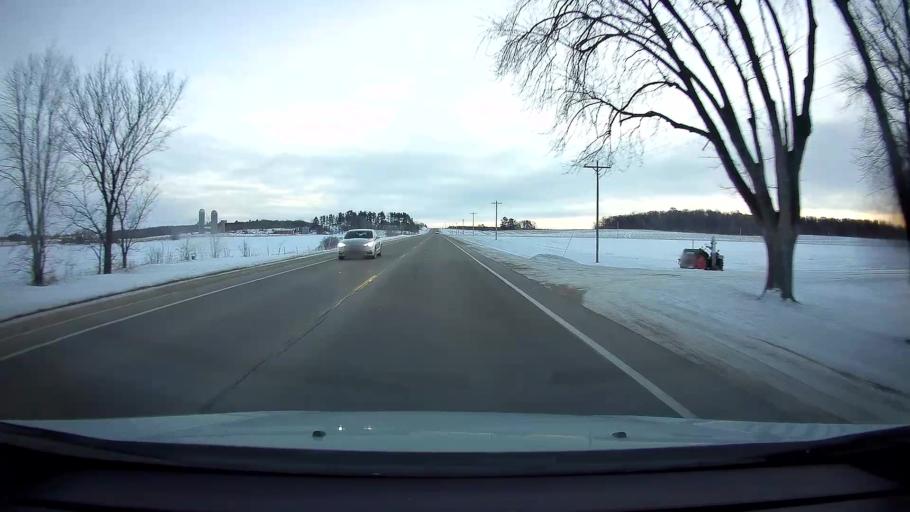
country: US
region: Wisconsin
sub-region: Saint Croix County
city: New Richmond
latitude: 45.1368
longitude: -92.4499
